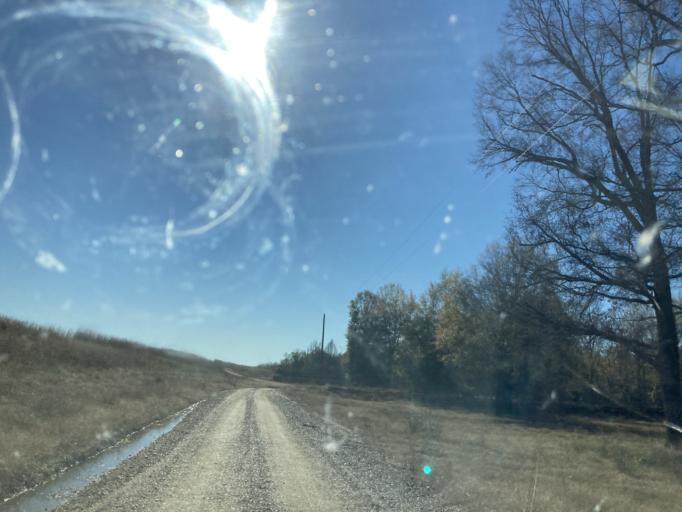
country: US
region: Mississippi
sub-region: Sharkey County
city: Rolling Fork
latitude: 32.7500
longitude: -90.6617
